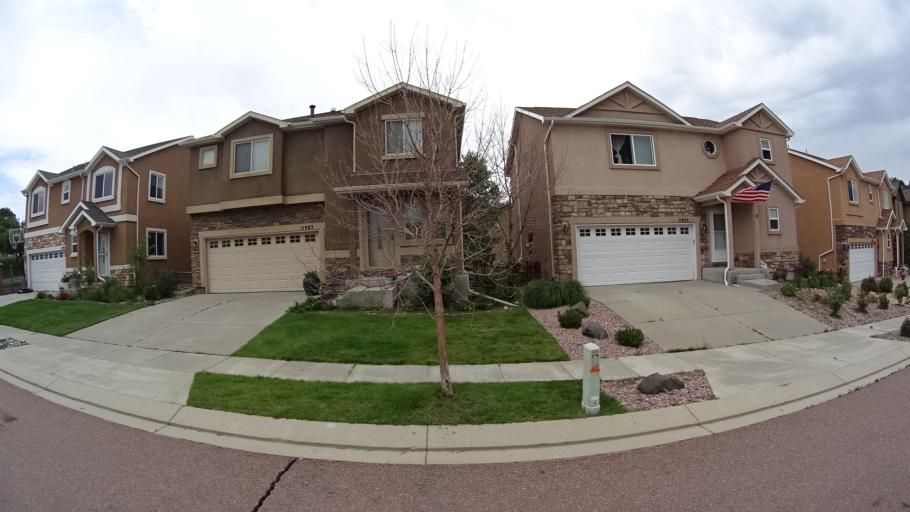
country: US
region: Colorado
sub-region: El Paso County
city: Gleneagle
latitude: 39.0039
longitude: -104.7953
